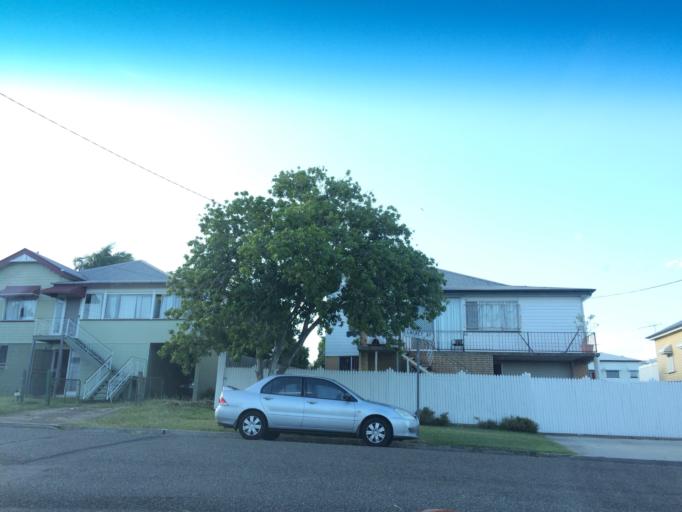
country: AU
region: Queensland
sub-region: Brisbane
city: Greenslopes
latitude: -27.4944
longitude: 153.0542
